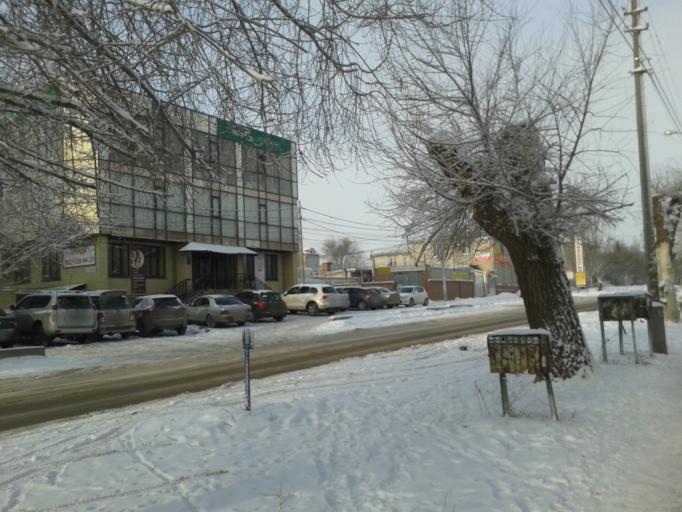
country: RU
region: Volgograd
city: Volgograd
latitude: 48.7230
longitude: 44.5107
